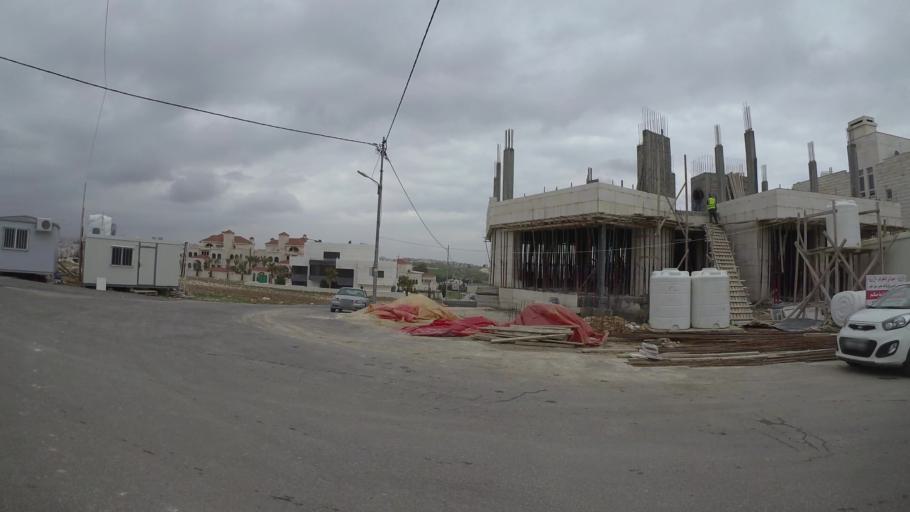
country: JO
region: Amman
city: Umm as Summaq
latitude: 31.9255
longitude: 35.8536
